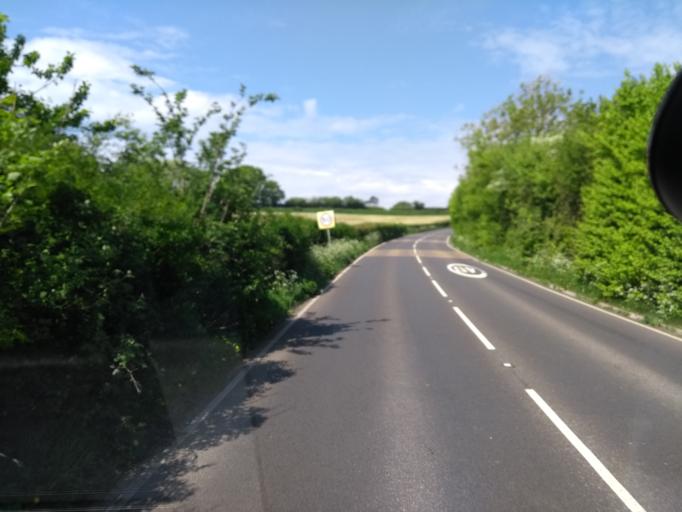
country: GB
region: England
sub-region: Somerset
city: Chard
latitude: 50.8738
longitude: -2.9780
